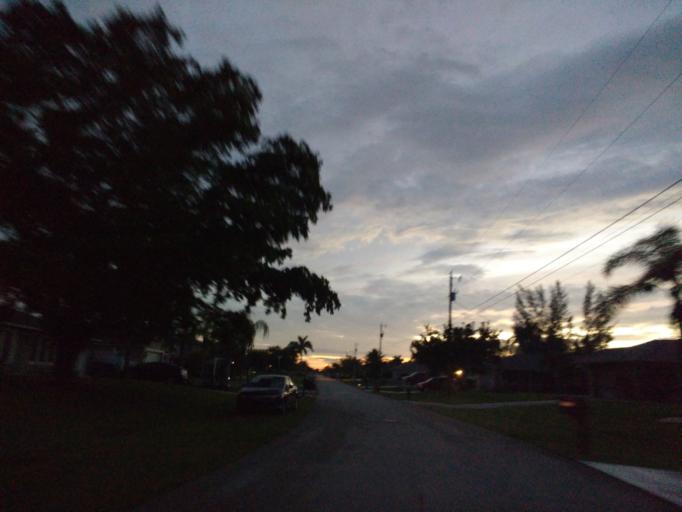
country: US
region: Florida
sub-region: Lee County
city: Lochmoor Waterway Estates
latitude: 26.6209
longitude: -81.9638
